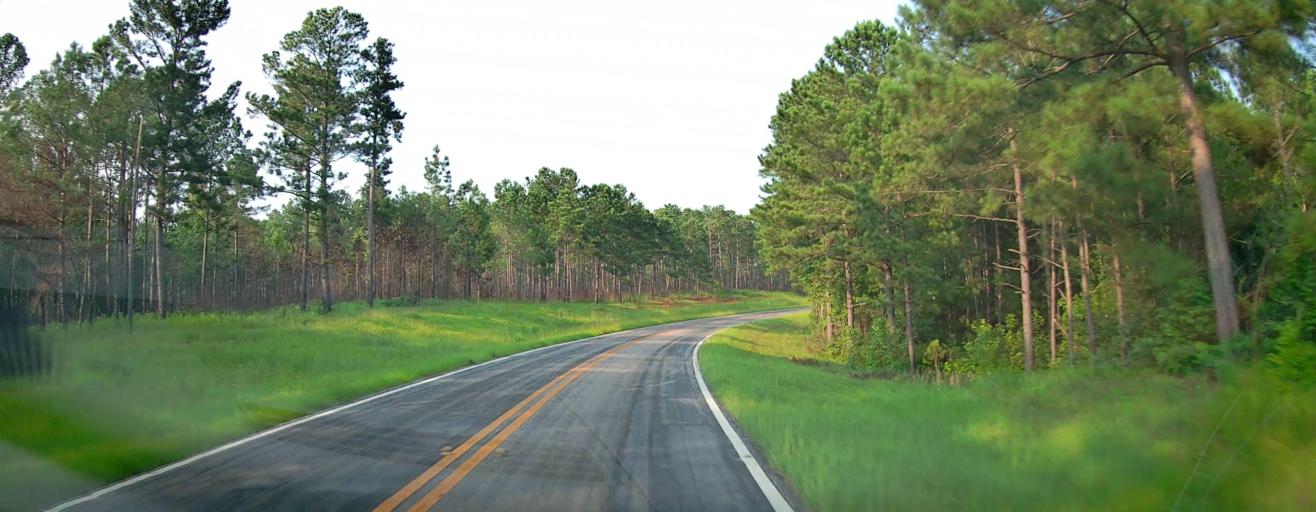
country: US
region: Georgia
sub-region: Jones County
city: Gray
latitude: 33.1132
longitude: -83.6551
